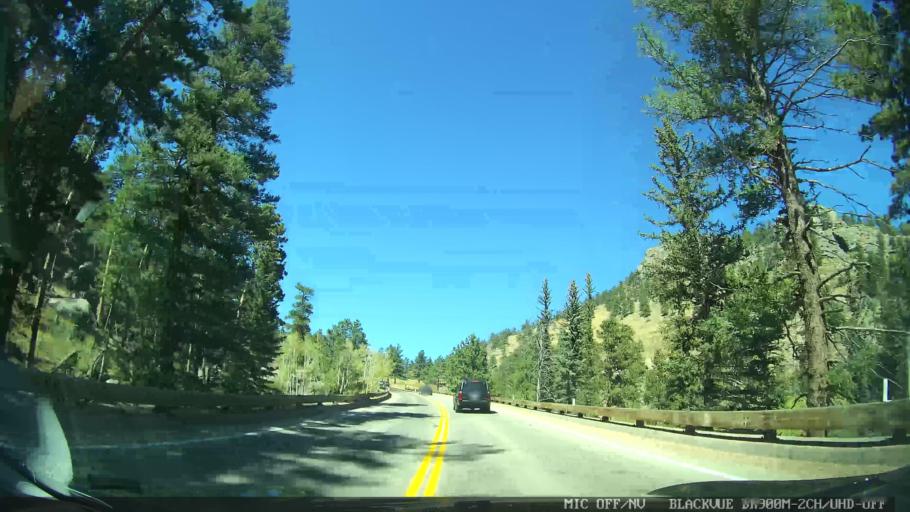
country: US
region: Colorado
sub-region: Larimer County
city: Estes Park
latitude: 40.3498
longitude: -105.5771
